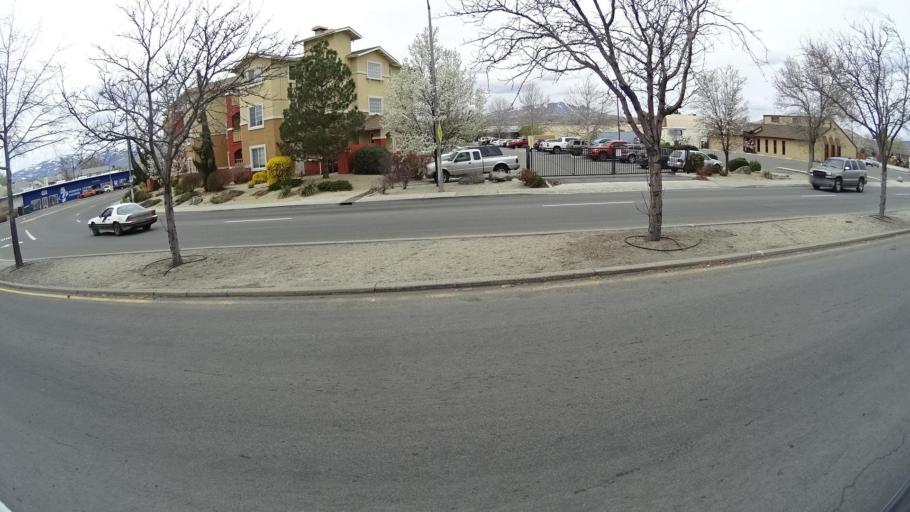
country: US
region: Nevada
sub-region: Washoe County
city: Sparks
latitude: 39.5444
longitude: -119.7621
